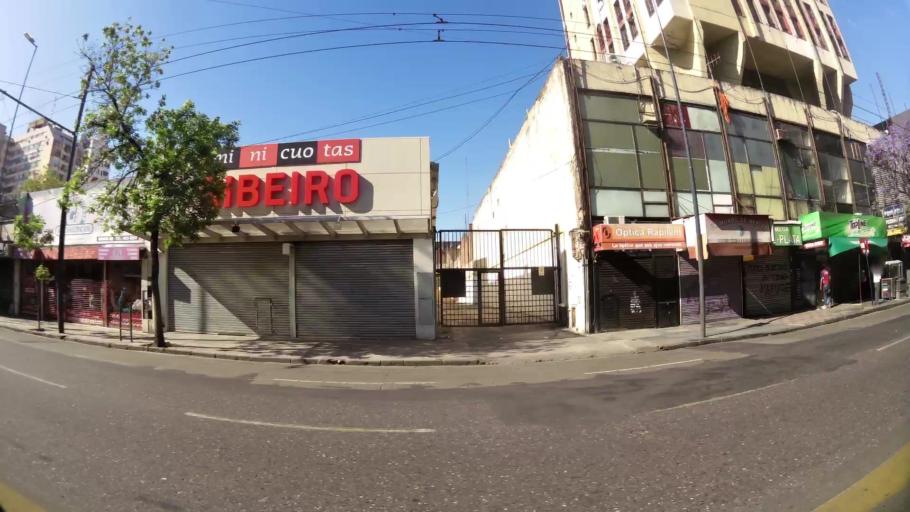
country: AR
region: Cordoba
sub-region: Departamento de Capital
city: Cordoba
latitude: -31.4139
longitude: -64.1825
